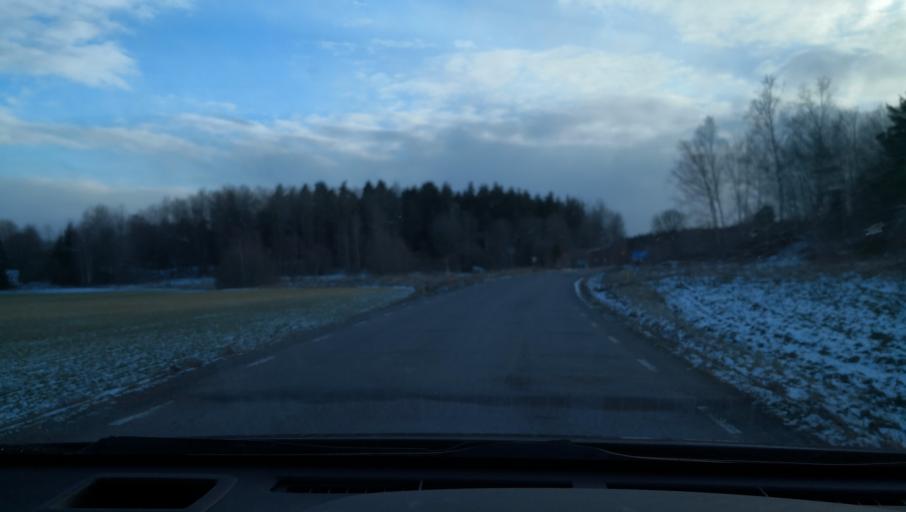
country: SE
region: Vaestmanland
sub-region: Vasteras
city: Tillberga
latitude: 59.6515
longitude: 16.7534
